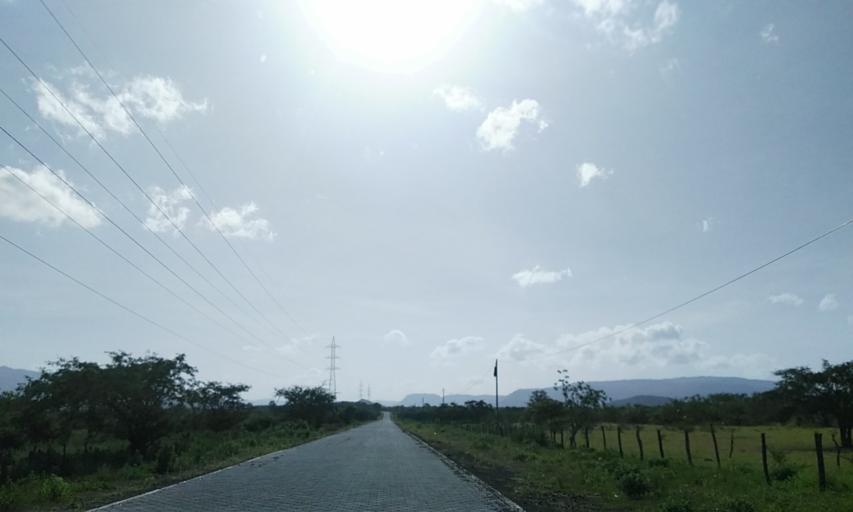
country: NI
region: Matagalpa
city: Ciudad Dario
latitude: 12.7247
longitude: -86.0958
